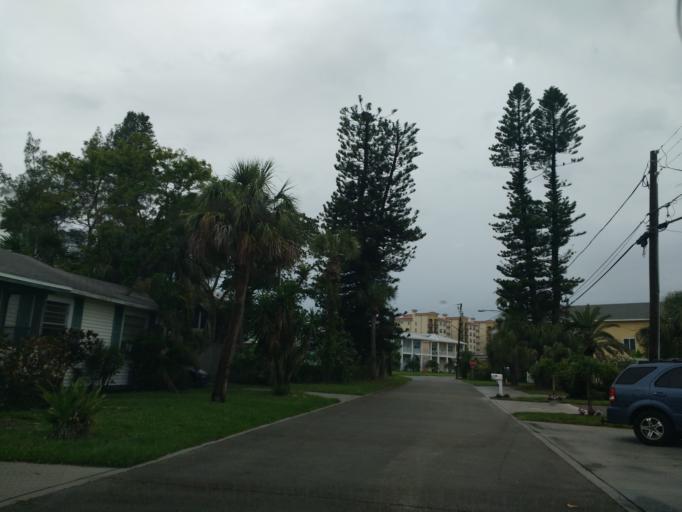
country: US
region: Florida
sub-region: Pinellas County
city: Madeira Beach
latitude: 27.7918
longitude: -82.7874
